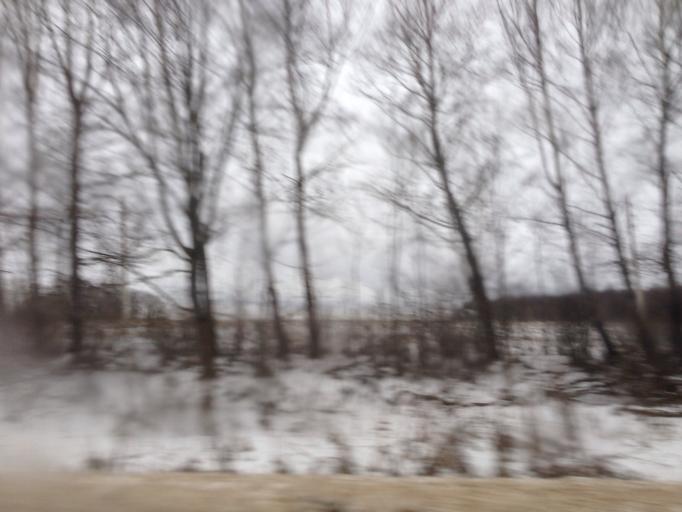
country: RU
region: Tula
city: Skuratovskiy
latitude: 54.1198
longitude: 37.7049
